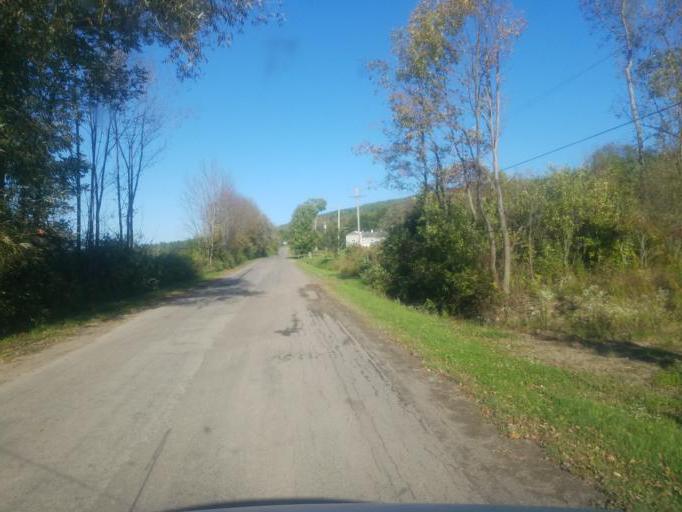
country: US
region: New York
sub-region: Allegany County
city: Cuba
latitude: 42.2688
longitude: -78.2032
